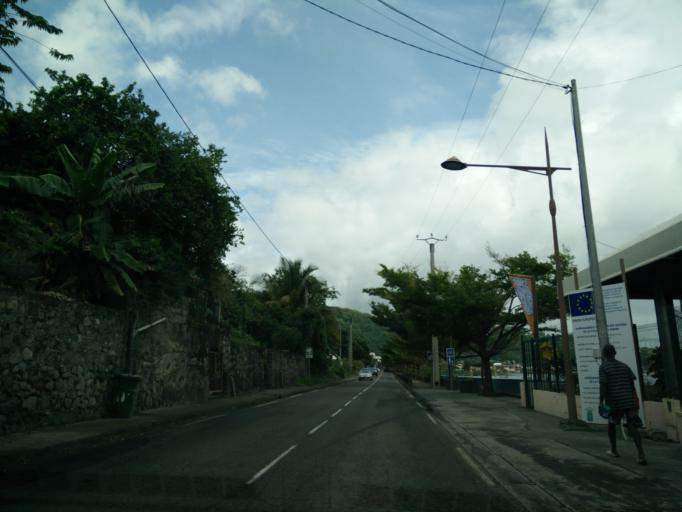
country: MQ
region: Martinique
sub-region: Martinique
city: Saint-Pierre
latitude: 14.7530
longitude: -61.1816
